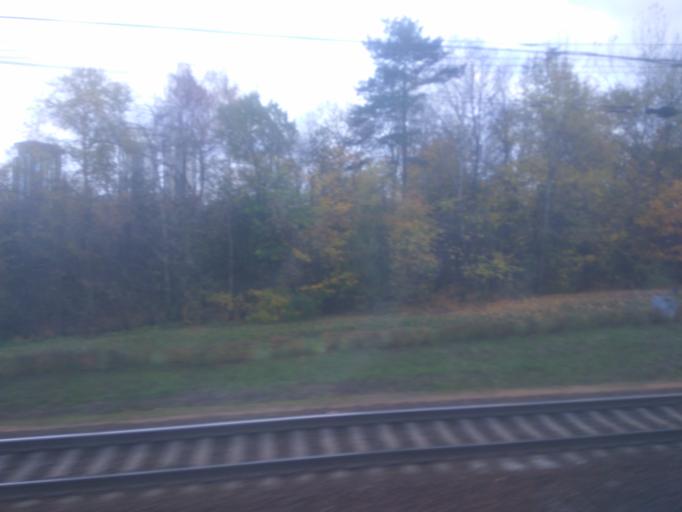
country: RU
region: Moskovskaya
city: Kastanayevo
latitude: 55.7145
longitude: 37.4933
